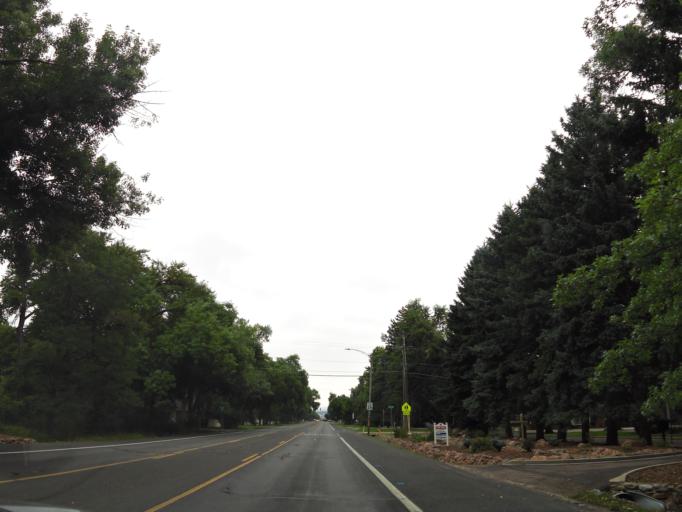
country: US
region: Colorado
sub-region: El Paso County
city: Colorado Springs
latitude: 38.7935
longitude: -104.8390
